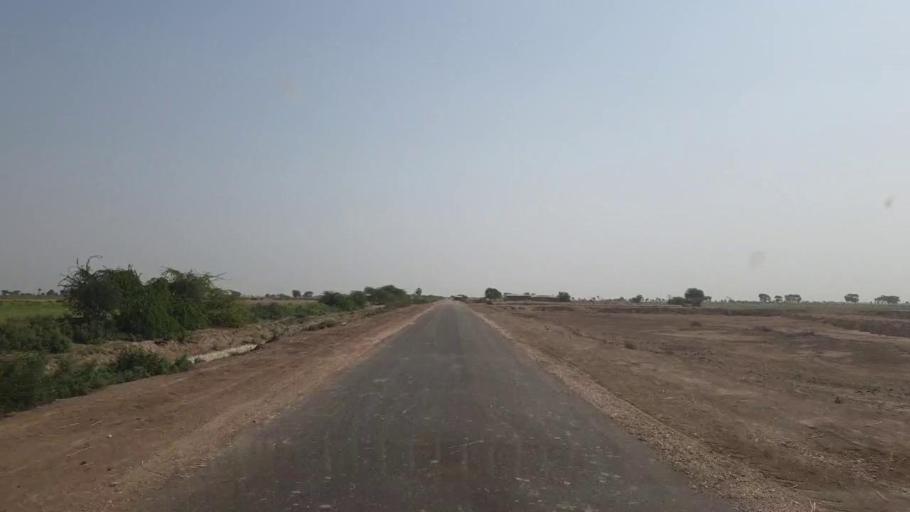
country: PK
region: Sindh
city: Jati
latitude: 24.4617
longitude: 68.5115
